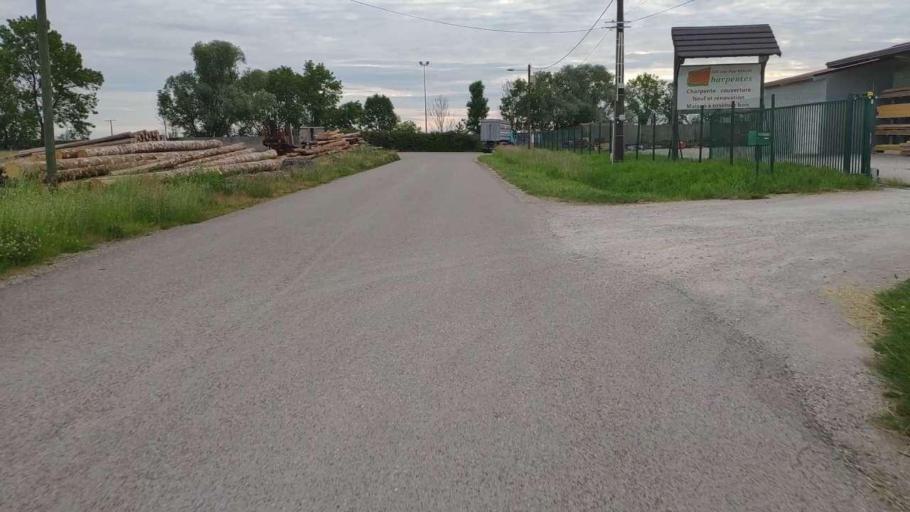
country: FR
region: Franche-Comte
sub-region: Departement du Jura
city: Bletterans
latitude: 46.7506
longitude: 5.4628
